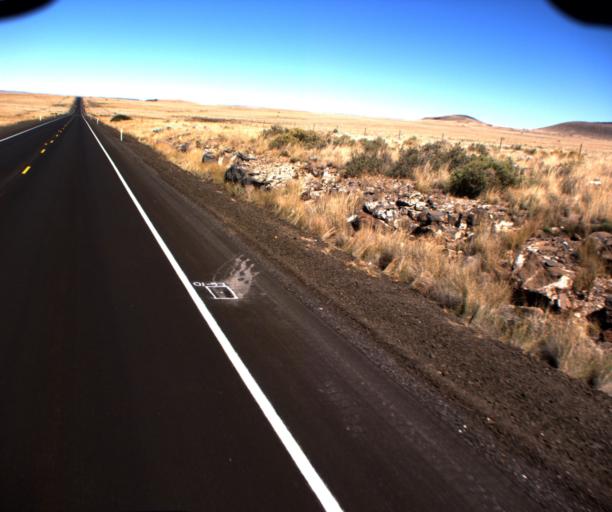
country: US
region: Arizona
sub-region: Apache County
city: Springerville
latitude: 34.2080
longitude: -109.3291
